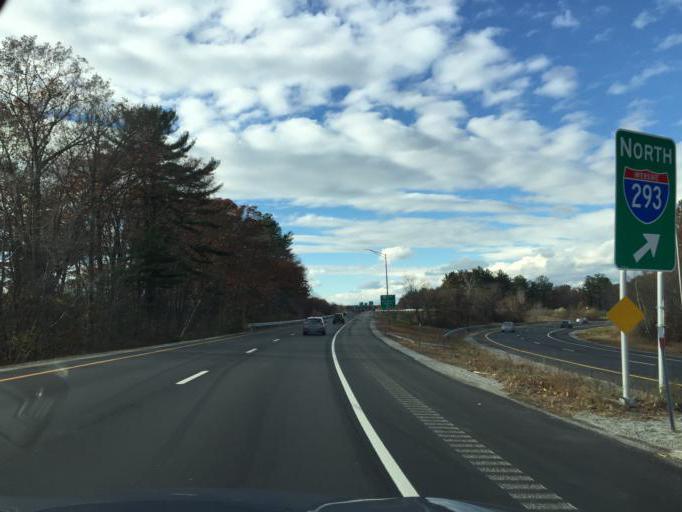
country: US
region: New Hampshire
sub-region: Hillsborough County
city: Bedford
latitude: 42.9470
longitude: -71.4675
